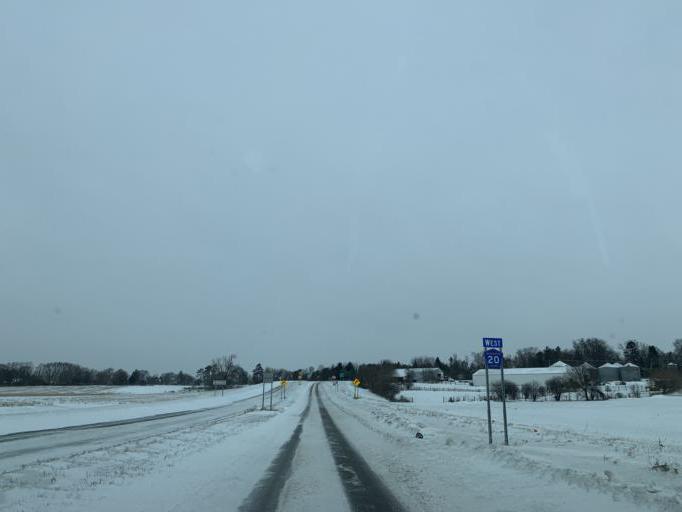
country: US
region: Minnesota
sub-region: Washington County
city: Cottage Grove
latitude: 44.8580
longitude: -92.9235
